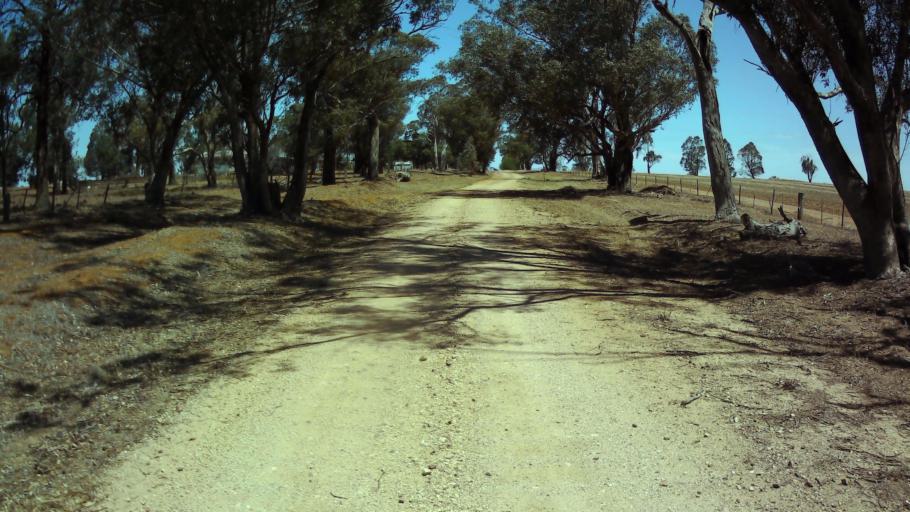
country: AU
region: New South Wales
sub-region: Weddin
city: Grenfell
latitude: -34.0149
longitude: 148.3520
